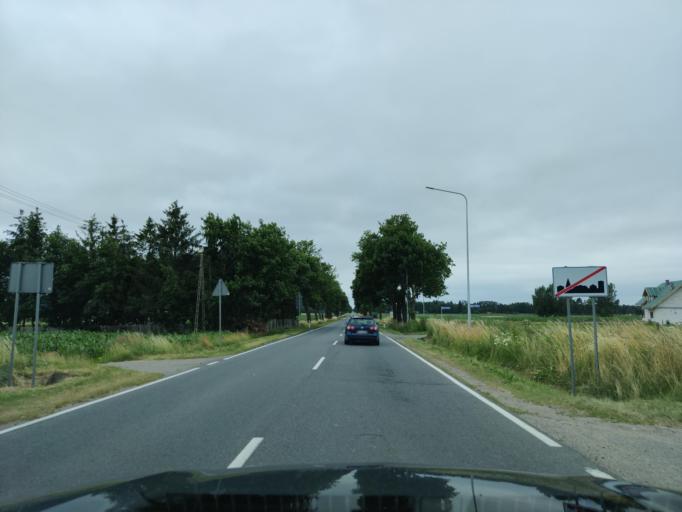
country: PL
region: Masovian Voivodeship
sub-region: Powiat ostrolecki
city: Myszyniec
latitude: 53.4309
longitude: 21.3620
